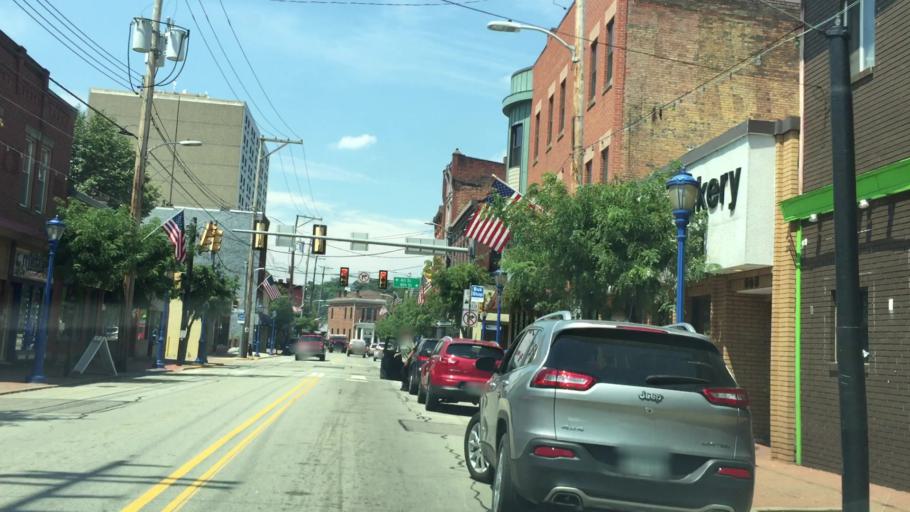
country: US
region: Pennsylvania
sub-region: Allegheny County
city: Sharpsburg
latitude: 40.4947
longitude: -79.9340
